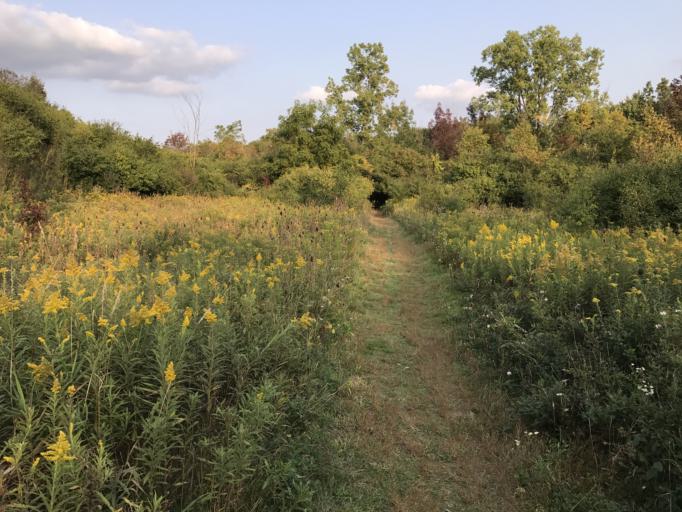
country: US
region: Michigan
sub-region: Oakland County
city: Farmington Hills
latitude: 42.4939
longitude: -83.3872
